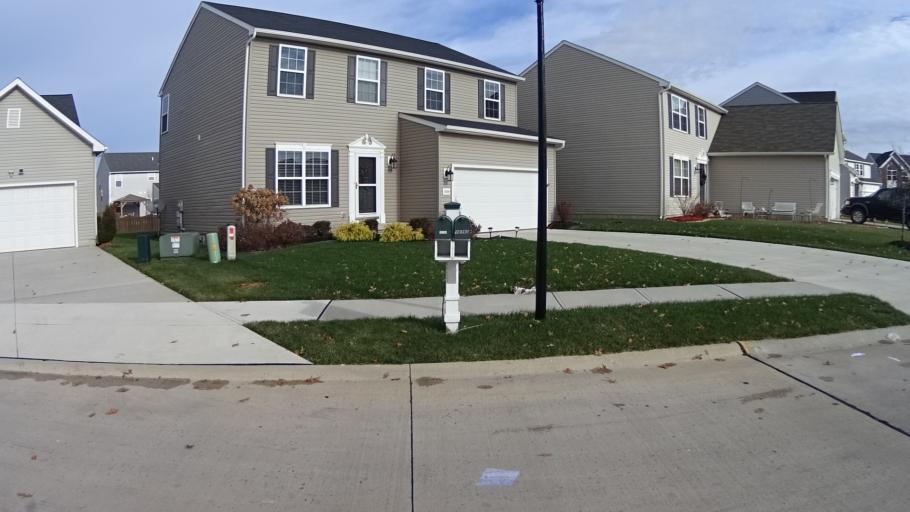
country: US
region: Ohio
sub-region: Lorain County
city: North Ridgeville
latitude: 41.3609
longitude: -82.0520
